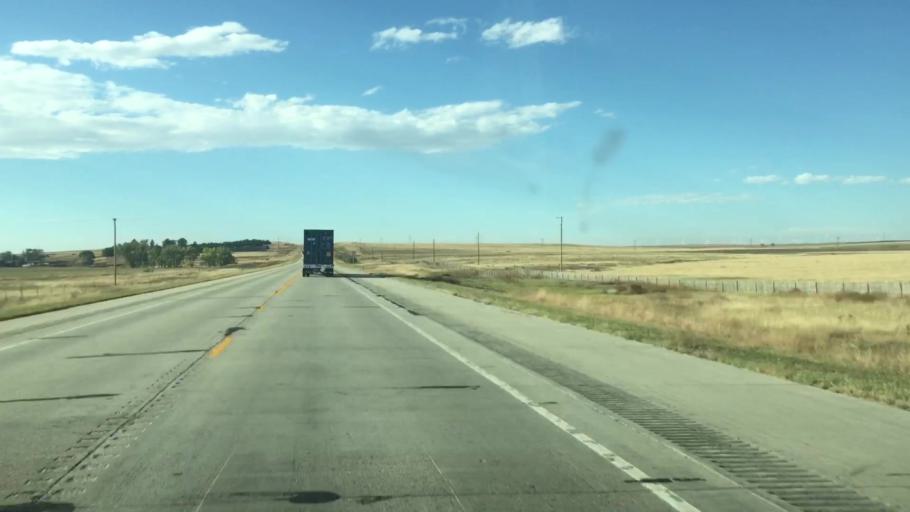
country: US
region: Colorado
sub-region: Lincoln County
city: Limon
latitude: 39.2365
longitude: -103.6216
